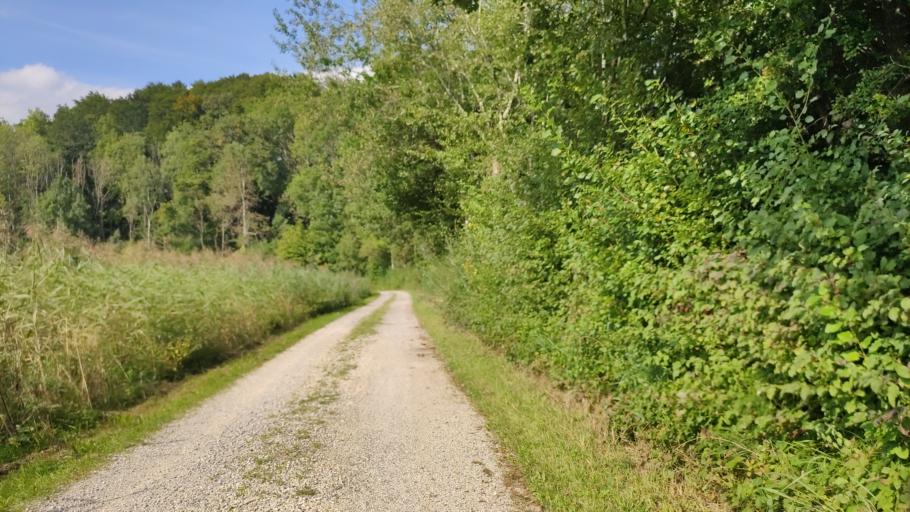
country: DE
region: Bavaria
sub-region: Upper Bavaria
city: Kaufering
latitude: 48.1188
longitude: 10.8605
